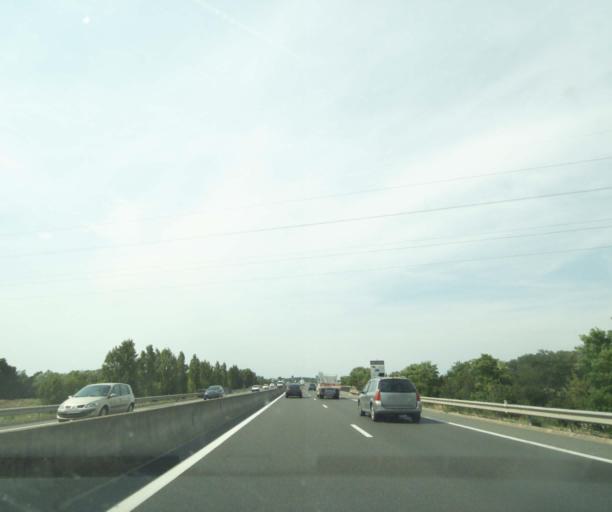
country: FR
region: Centre
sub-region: Departement d'Indre-et-Loire
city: Joue-les-Tours
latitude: 47.3711
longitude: 0.6541
